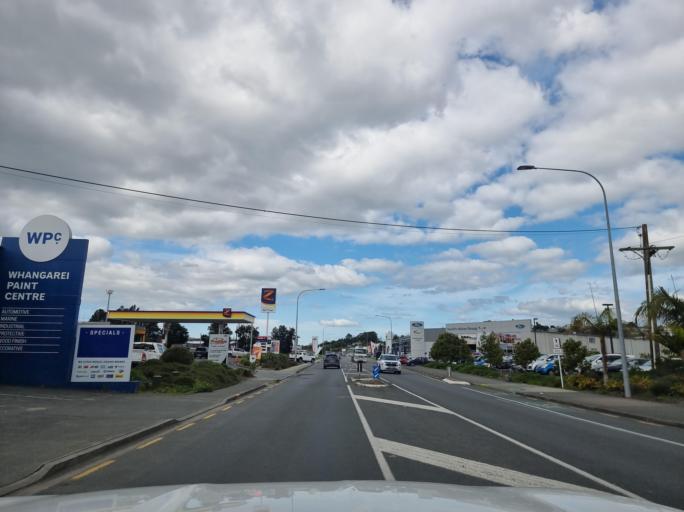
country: NZ
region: Northland
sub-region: Whangarei
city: Whangarei
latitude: -35.7321
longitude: 174.3216
